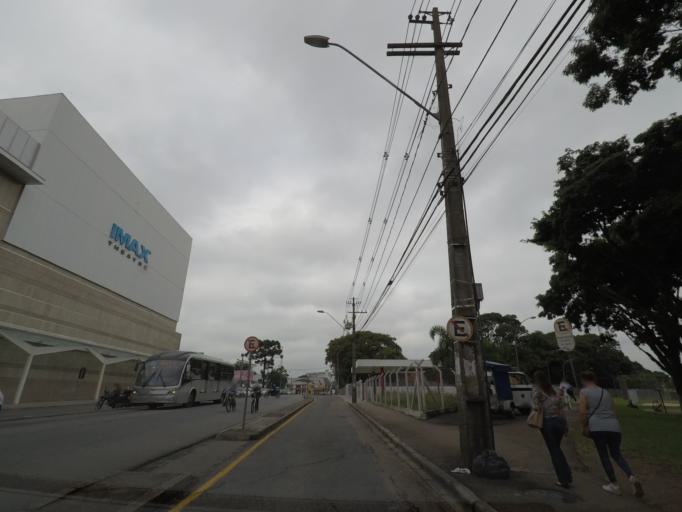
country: BR
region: Parana
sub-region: Curitiba
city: Curitiba
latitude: -25.4782
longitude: -49.2922
